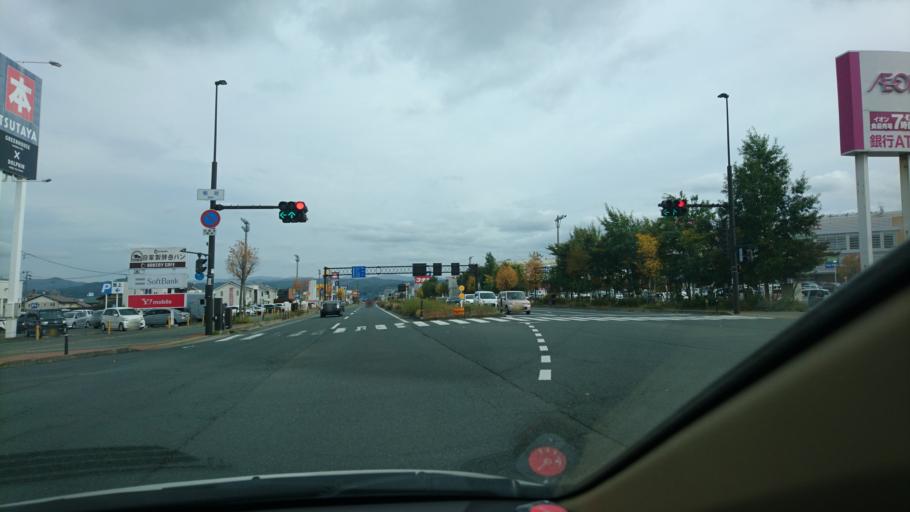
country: JP
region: Iwate
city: Morioka-shi
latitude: 39.6852
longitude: 141.1262
